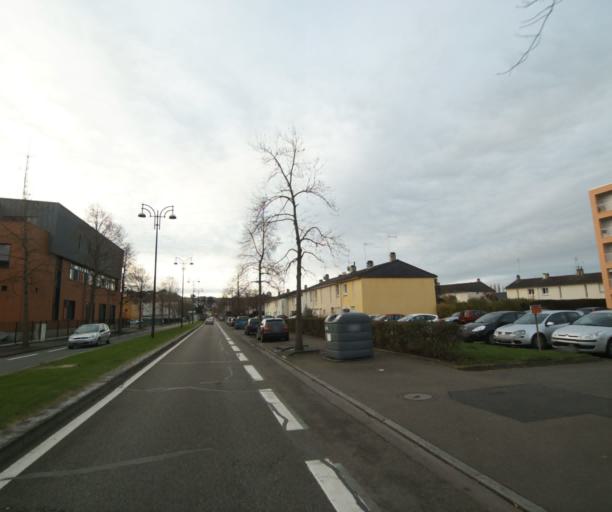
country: FR
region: Pays de la Loire
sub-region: Departement de la Sarthe
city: Coulaines
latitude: 48.0207
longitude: 0.2016
